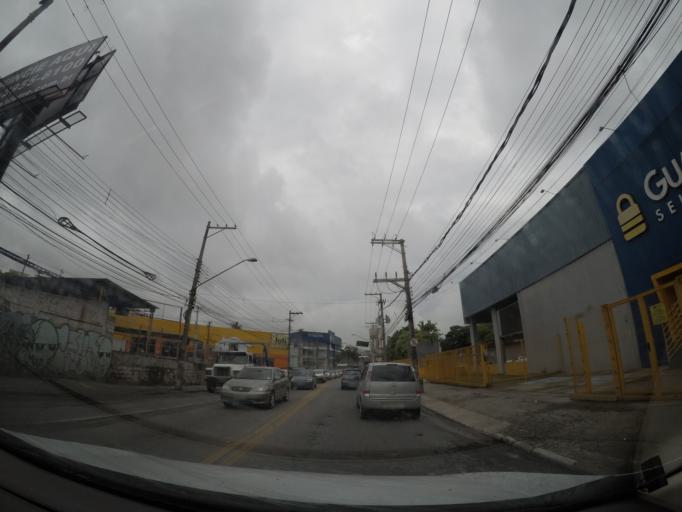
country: BR
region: Sao Paulo
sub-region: Guarulhos
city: Guarulhos
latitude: -23.4666
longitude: -46.5147
